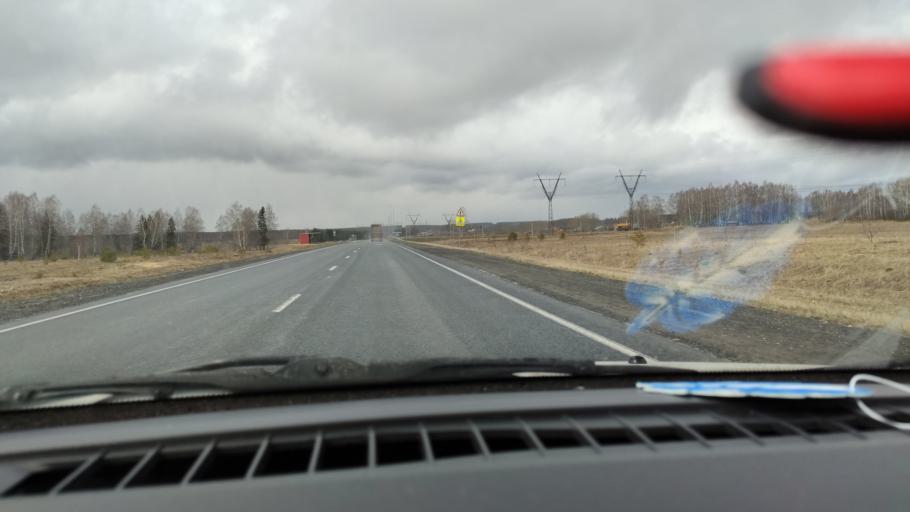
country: RU
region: Perm
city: Orda
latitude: 57.2543
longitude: 57.0344
